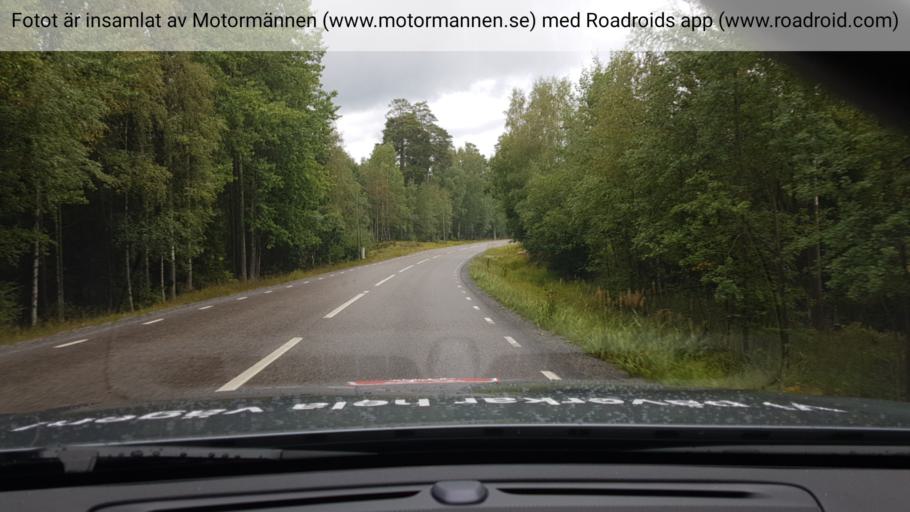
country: SE
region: Stockholm
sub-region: Botkyrka Kommun
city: Tullinge
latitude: 59.1772
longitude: 17.9289
